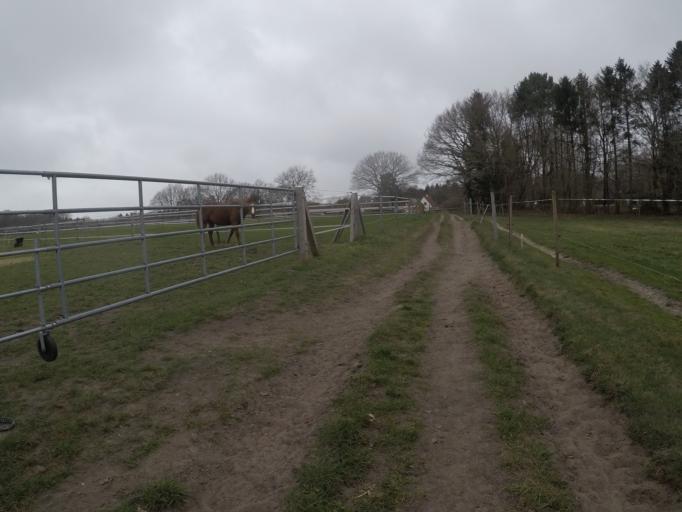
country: DE
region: Lower Saxony
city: Cuxhaven
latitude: 53.8404
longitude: 8.6429
